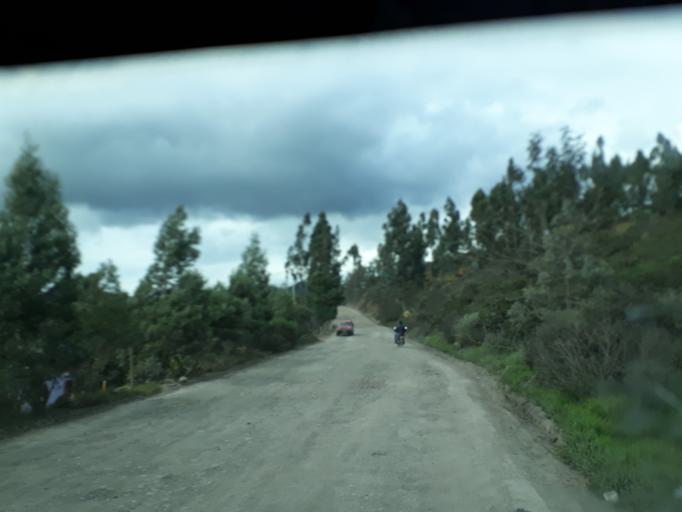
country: CO
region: Cundinamarca
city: Cucunuba
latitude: 5.2456
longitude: -73.7920
